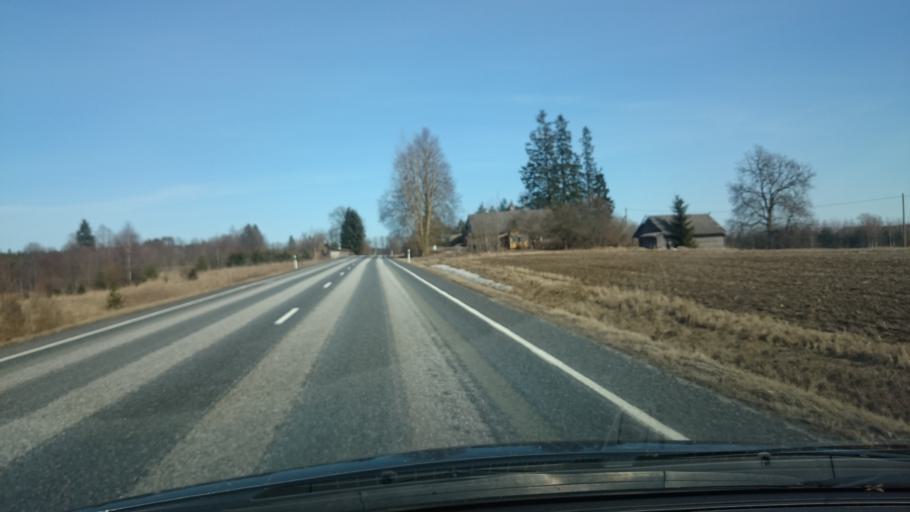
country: EE
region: Jaervamaa
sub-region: Tueri vald
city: Sarevere
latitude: 58.7488
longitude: 25.3172
